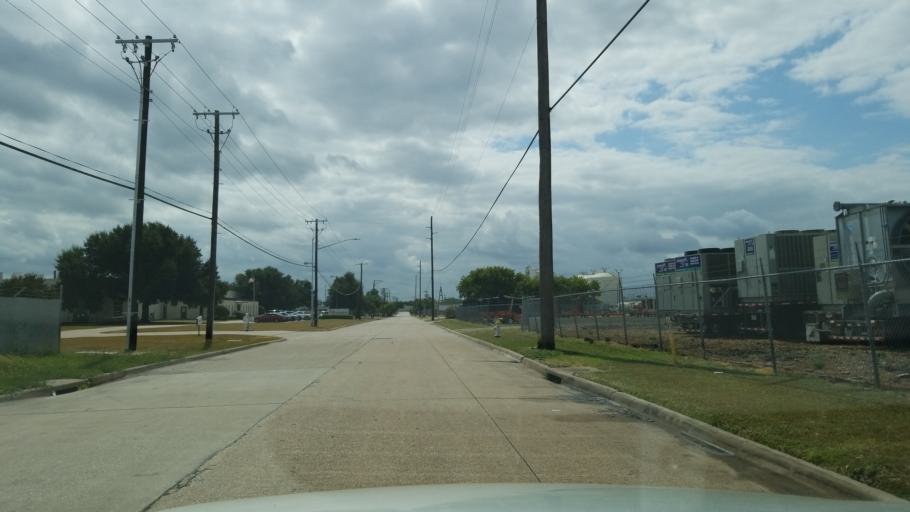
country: US
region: Texas
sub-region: Dallas County
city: Garland
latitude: 32.8925
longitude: -96.6734
